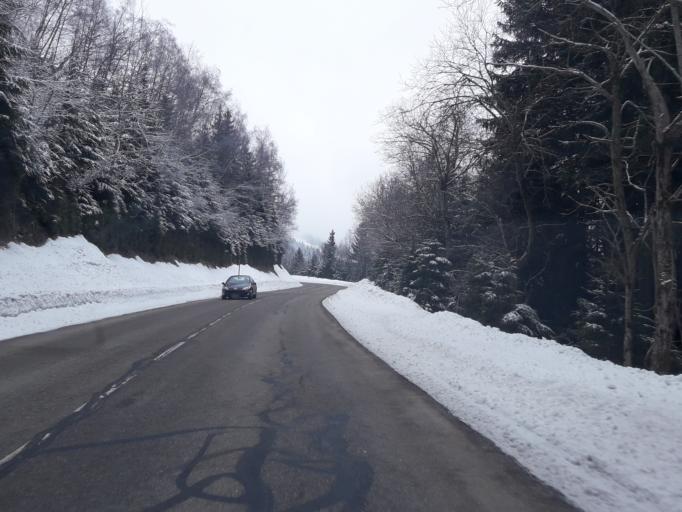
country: FR
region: Rhone-Alpes
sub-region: Departement de l'Isere
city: Theys
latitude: 45.2689
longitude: 6.0066
